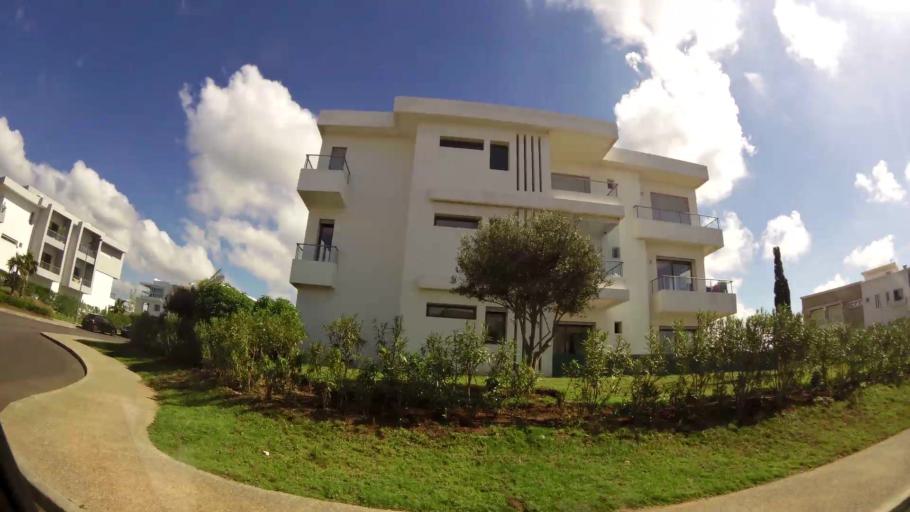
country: MA
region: Grand Casablanca
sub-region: Nouaceur
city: Bouskoura
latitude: 33.4719
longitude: -7.6057
